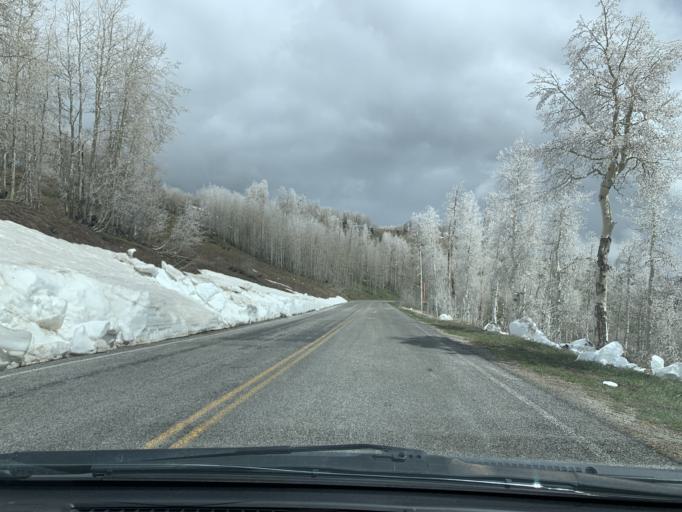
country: US
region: Utah
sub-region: Utah County
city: Santaquin
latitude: 39.8512
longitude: -111.7028
